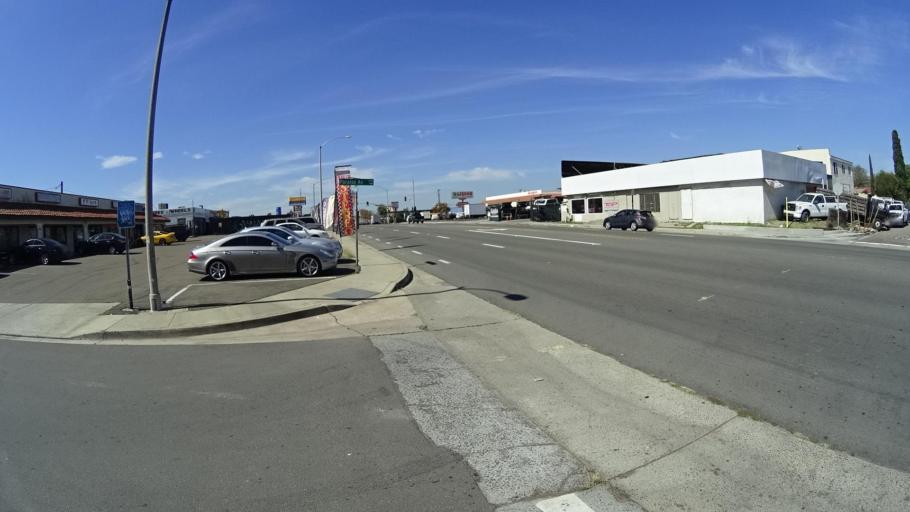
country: US
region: California
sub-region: San Diego County
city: La Presa
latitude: 32.7077
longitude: -116.9962
